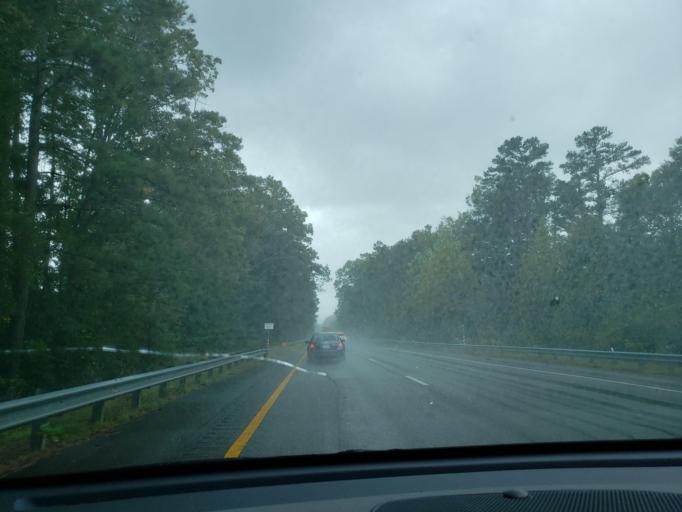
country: US
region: Virginia
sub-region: Mecklenburg County
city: South Hill
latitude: 36.7077
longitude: -78.1161
